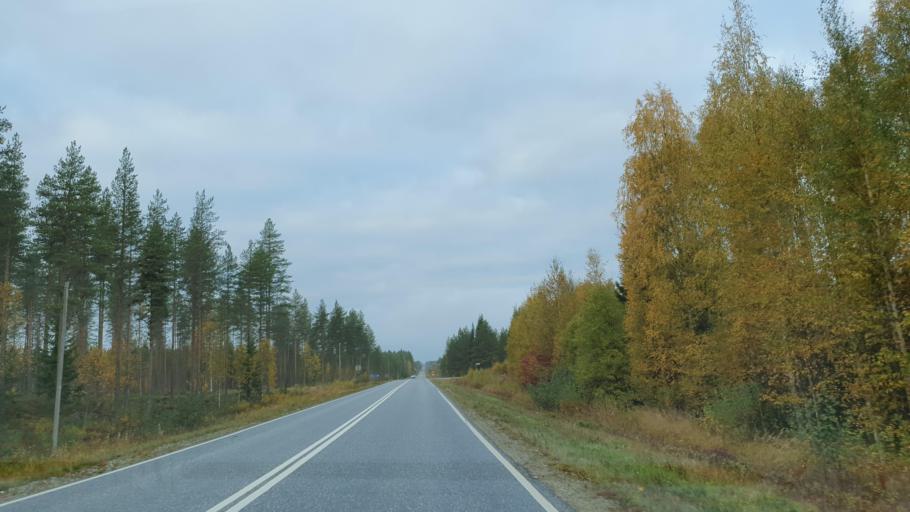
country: FI
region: Kainuu
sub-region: Kajaani
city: Sotkamo
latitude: 64.1620
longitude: 28.7257
